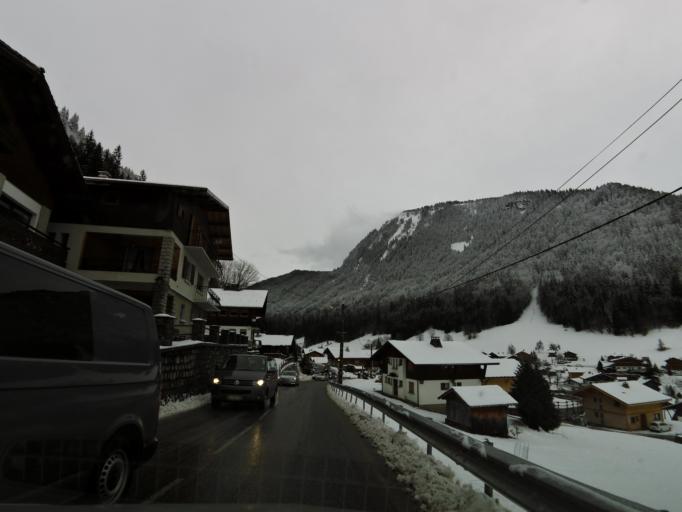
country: FR
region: Rhone-Alpes
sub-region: Departement de la Haute-Savoie
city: Morzine
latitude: 46.1820
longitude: 6.7128
